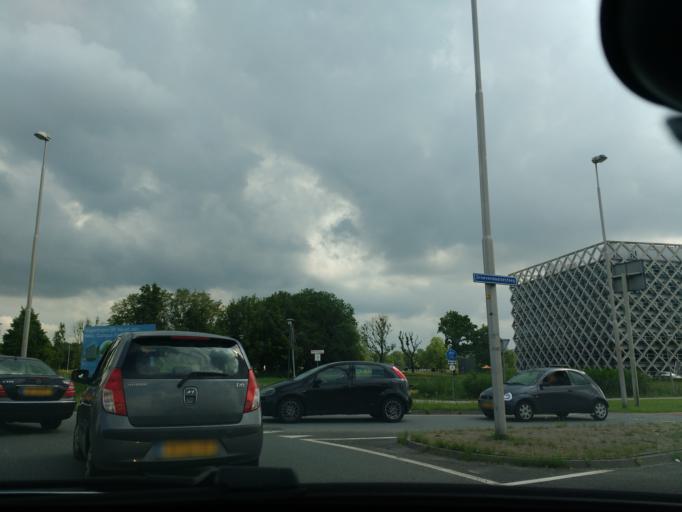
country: NL
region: Gelderland
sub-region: Gemeente Ede
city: Bennekom
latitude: 51.9876
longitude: 5.6690
